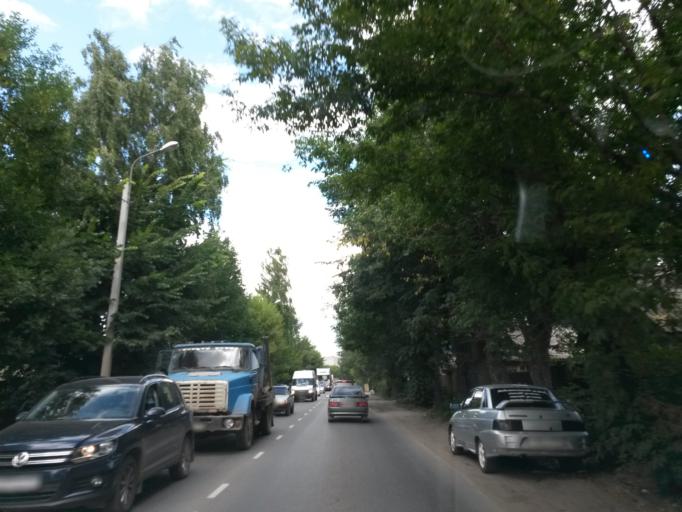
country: RU
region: Ivanovo
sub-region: Gorod Ivanovo
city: Ivanovo
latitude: 56.9907
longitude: 40.9528
